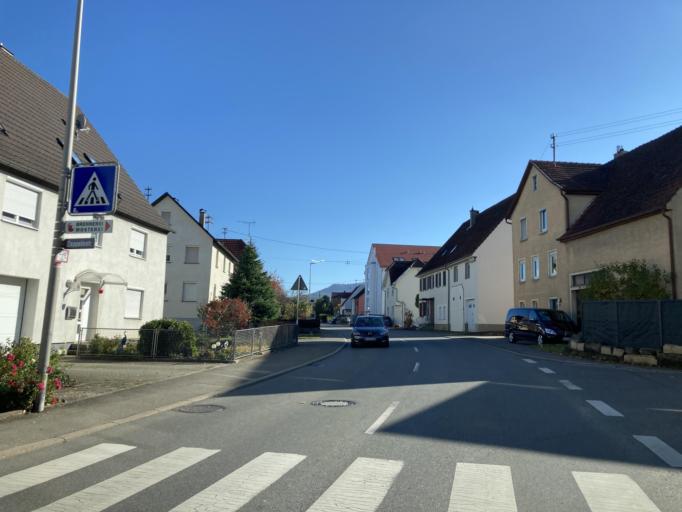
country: DE
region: Baden-Wuerttemberg
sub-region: Tuebingen Region
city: Ofterdingen
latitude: 48.4186
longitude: 9.0344
